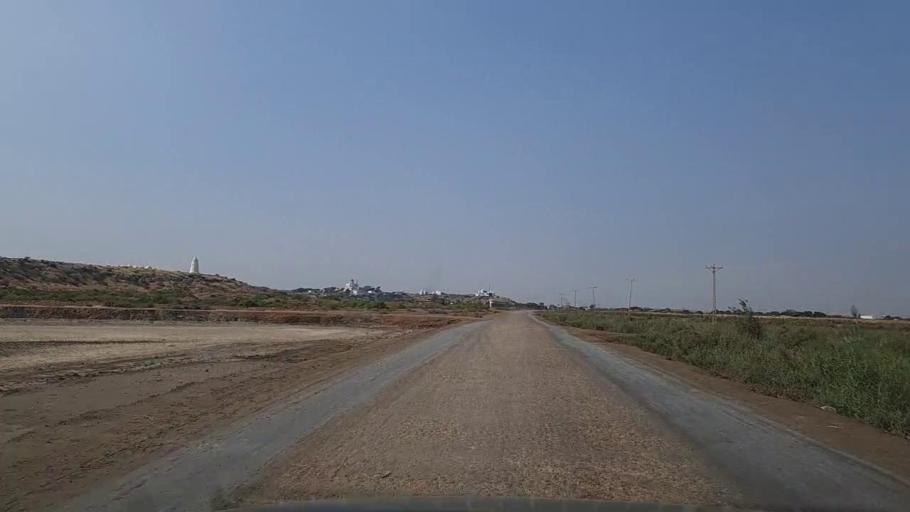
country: PK
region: Sindh
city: Chuhar Jamali
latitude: 24.5537
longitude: 67.8902
